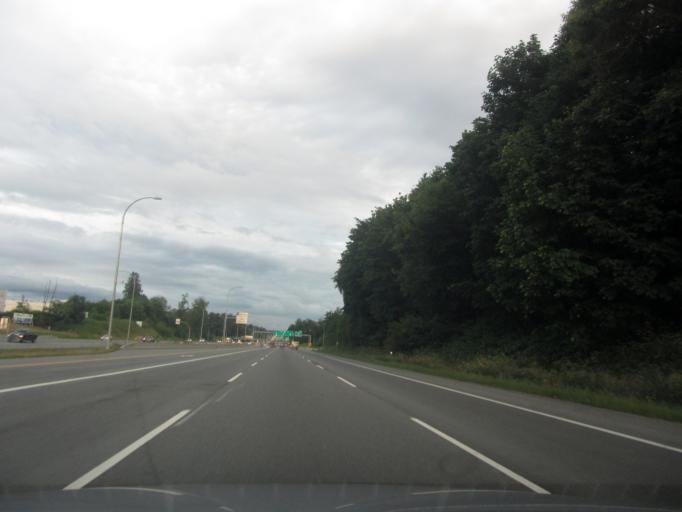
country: CA
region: British Columbia
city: Pitt Meadows
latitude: 49.1724
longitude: -122.7012
